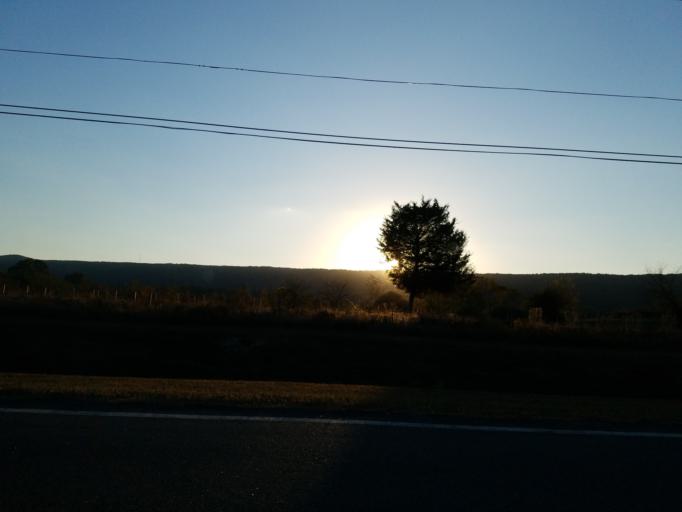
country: US
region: Georgia
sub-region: Gordon County
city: Calhoun
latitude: 34.5901
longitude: -85.0371
